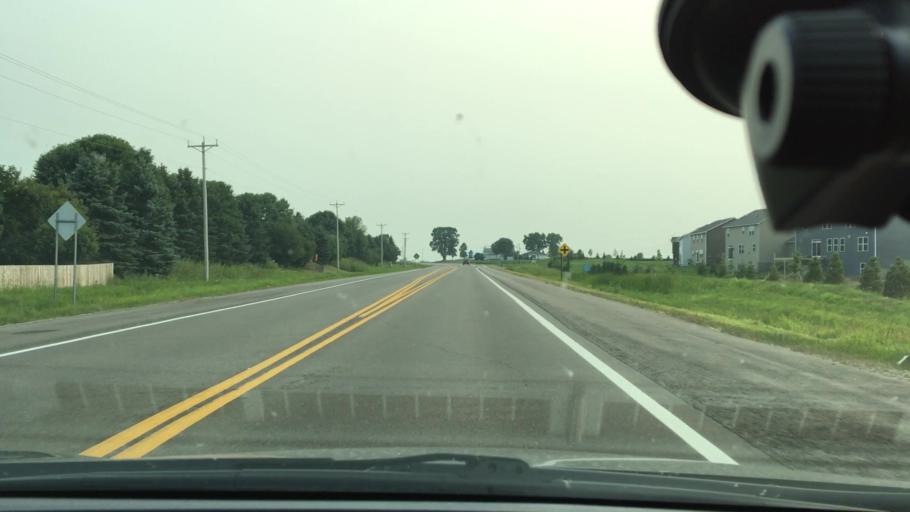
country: US
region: Minnesota
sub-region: Wright County
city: Saint Michael
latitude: 45.2048
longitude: -93.6793
